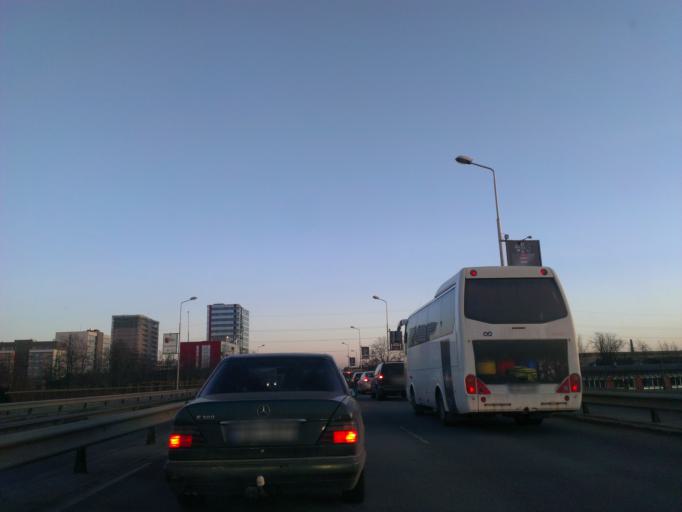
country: LV
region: Riga
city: Jaunciems
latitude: 56.9801
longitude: 24.1626
